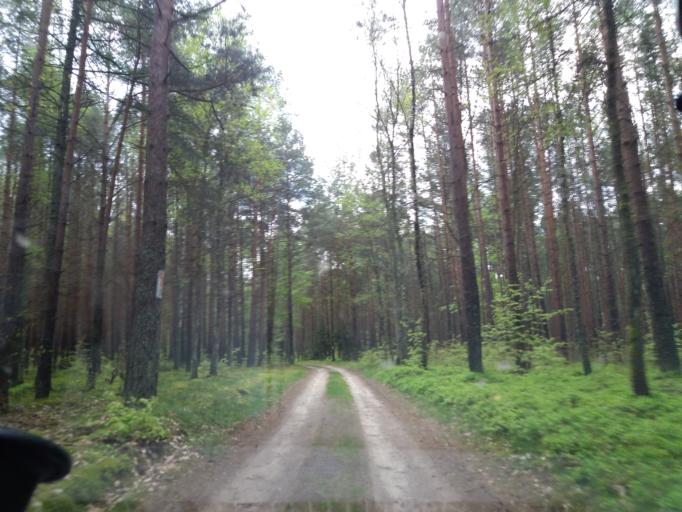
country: PL
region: West Pomeranian Voivodeship
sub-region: Powiat choszczenski
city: Drawno
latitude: 53.1142
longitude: 15.8655
